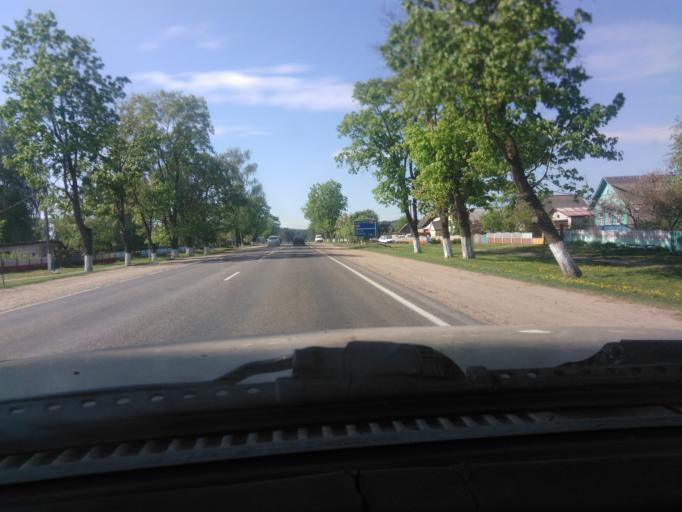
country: BY
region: Mogilev
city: Buynichy
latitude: 53.8250
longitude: 30.2413
